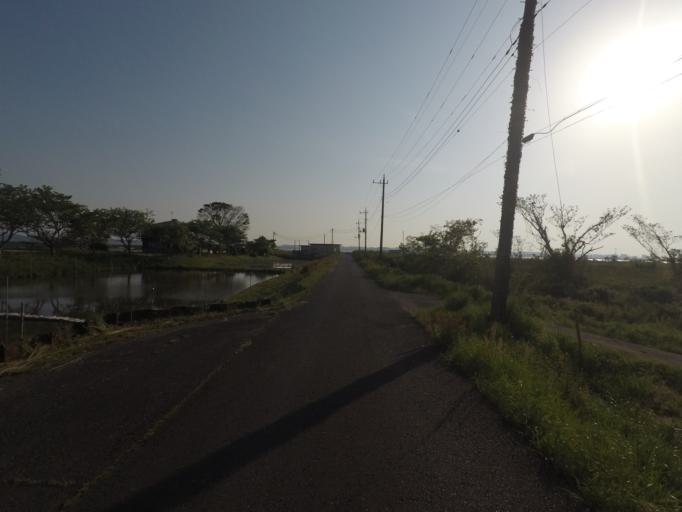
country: JP
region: Ibaraki
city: Ami
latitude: 36.0731
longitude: 140.2424
